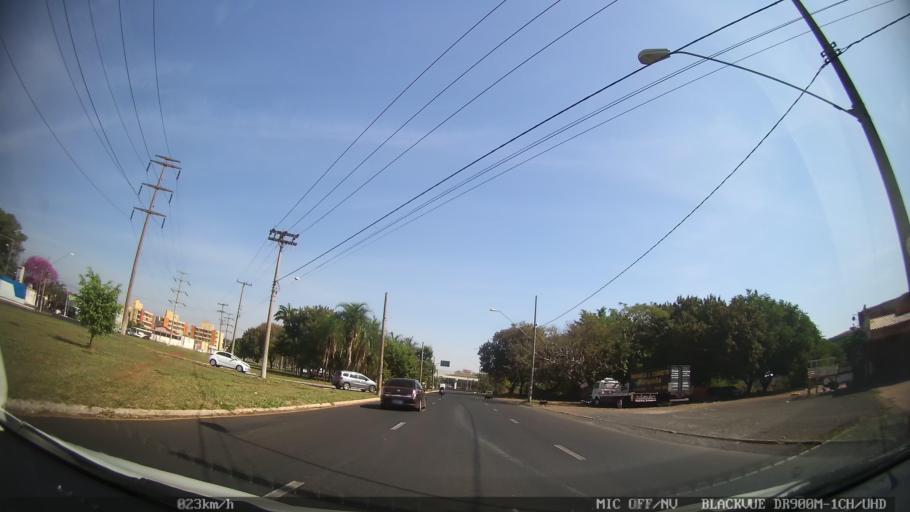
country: BR
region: Sao Paulo
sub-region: Ribeirao Preto
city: Ribeirao Preto
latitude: -21.1775
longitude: -47.8217
